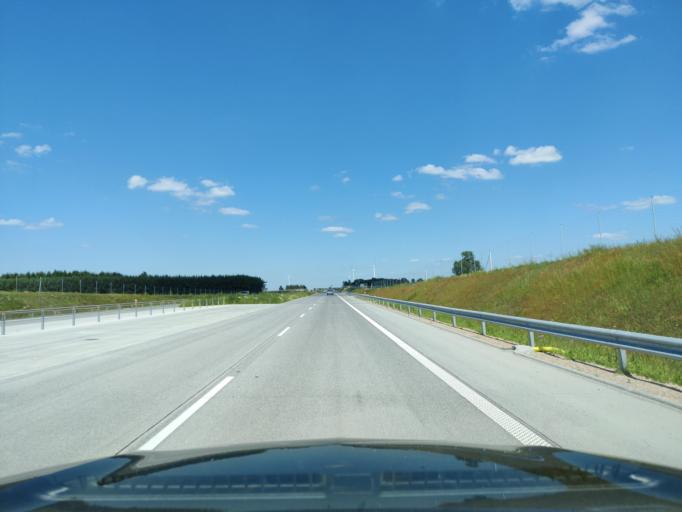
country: PL
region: Masovian Voivodeship
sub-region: Powiat mlawski
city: Wisniewo
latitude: 53.0275
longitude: 20.3476
